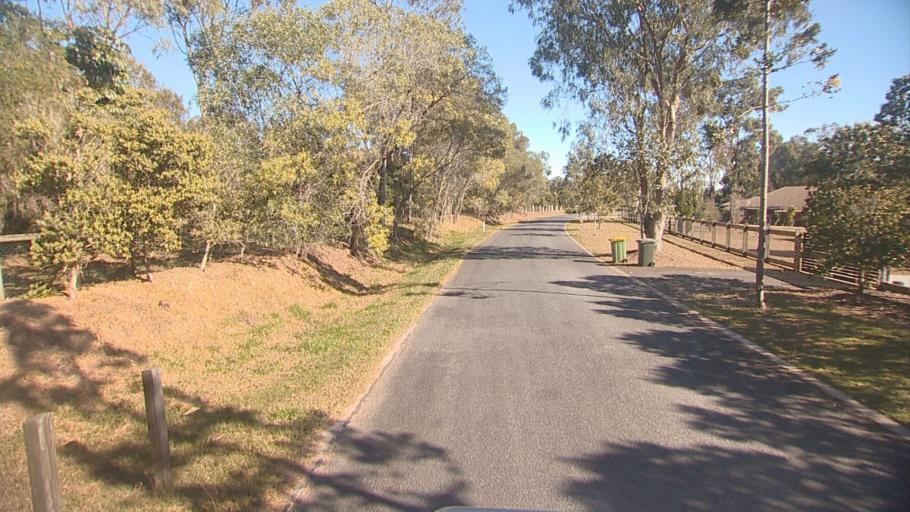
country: AU
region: Queensland
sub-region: Logan
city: North Maclean
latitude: -27.7381
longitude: 152.9595
